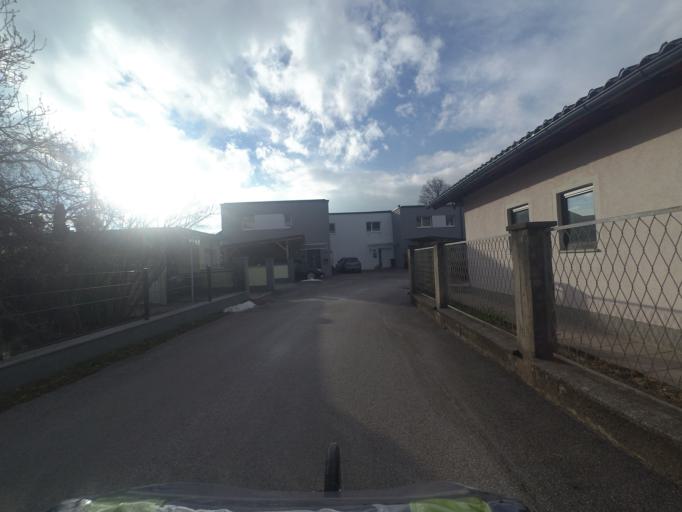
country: AT
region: Salzburg
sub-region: Politischer Bezirk Hallein
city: Puch bei Hallein
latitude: 47.7300
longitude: 13.0787
